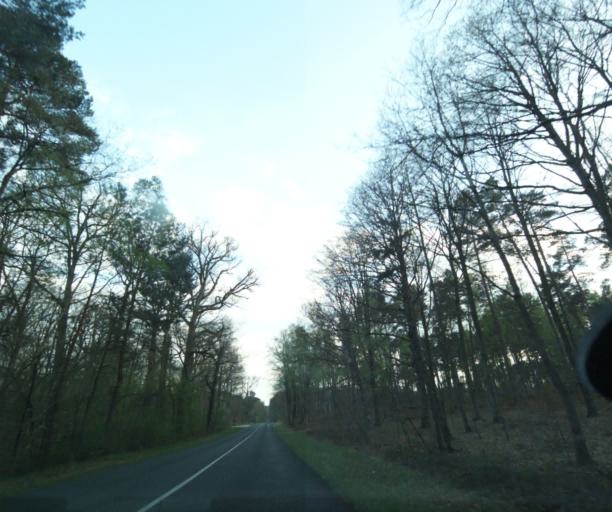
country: FR
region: Ile-de-France
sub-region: Departement de Seine-et-Marne
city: Veneux-les-Sablons
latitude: 48.3675
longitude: 2.7613
